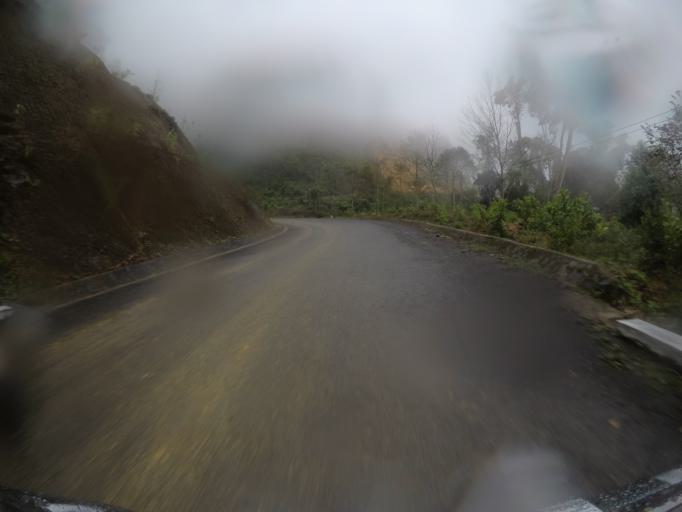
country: LA
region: Xekong
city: Dak Cheung
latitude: 15.5589
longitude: 107.3971
